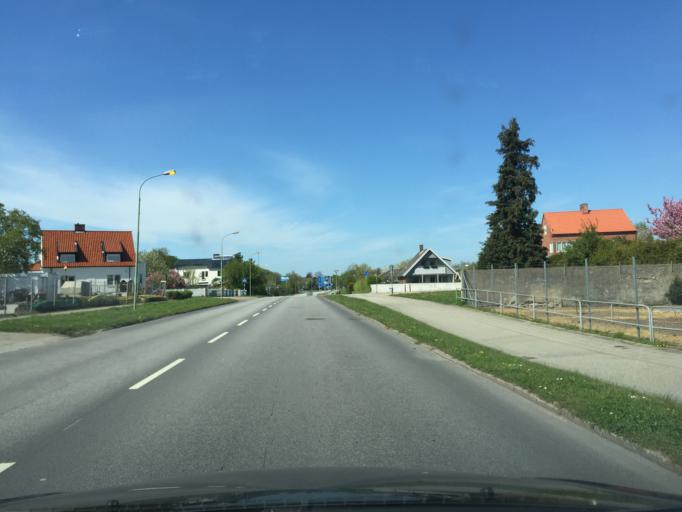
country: SE
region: Skane
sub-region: Skurups Kommun
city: Skurup
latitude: 55.4808
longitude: 13.5031
